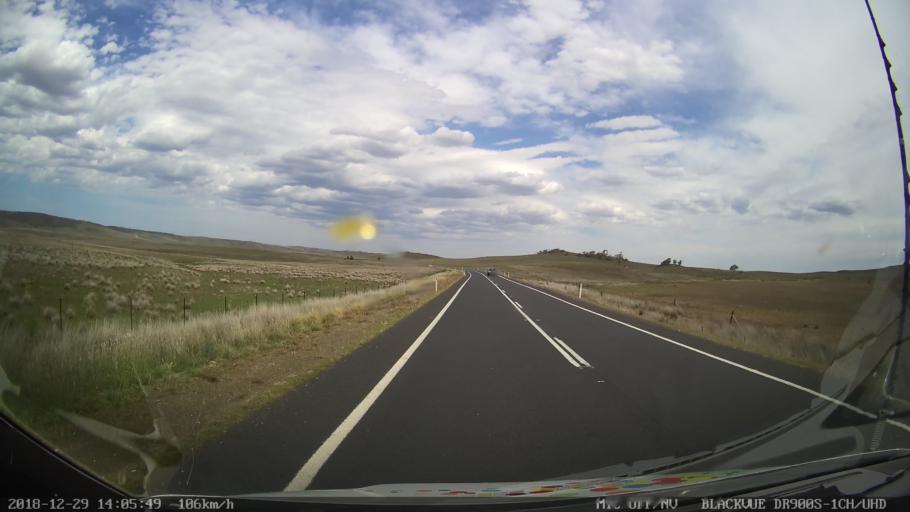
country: AU
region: New South Wales
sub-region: Cooma-Monaro
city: Cooma
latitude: -36.3358
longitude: 149.1946
